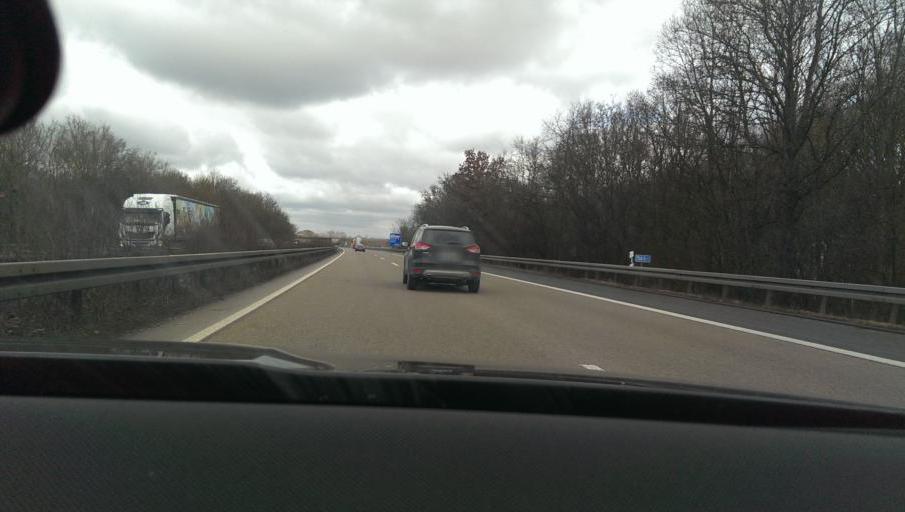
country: DE
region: Hesse
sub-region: Regierungsbezirk Kassel
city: Kunzell
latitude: 50.5486
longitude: 9.7313
